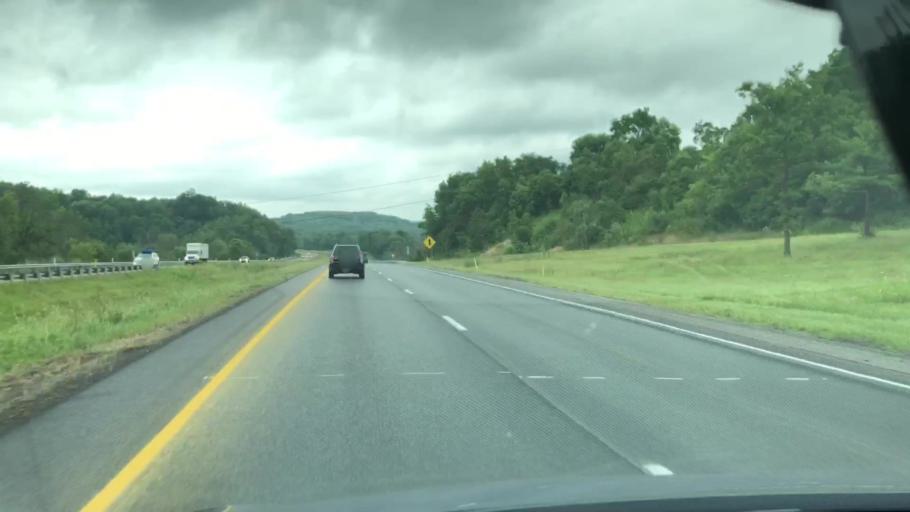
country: US
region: Pennsylvania
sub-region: Butler County
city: Prospect
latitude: 40.9221
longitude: -80.1328
